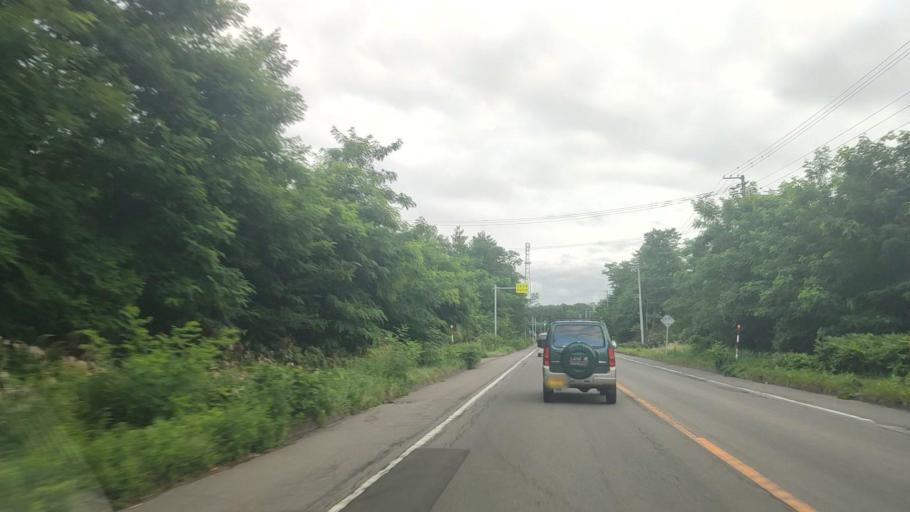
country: JP
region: Hokkaido
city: Nanae
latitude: 42.0689
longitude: 140.6032
